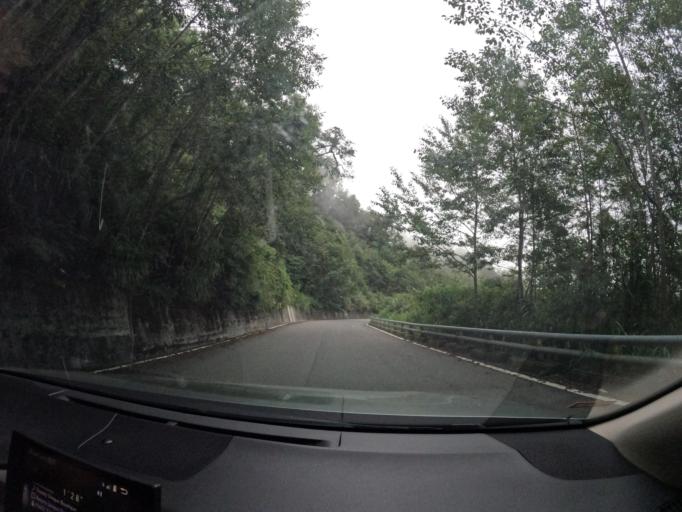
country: TW
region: Taiwan
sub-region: Taitung
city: Taitung
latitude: 23.2403
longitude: 120.9877
